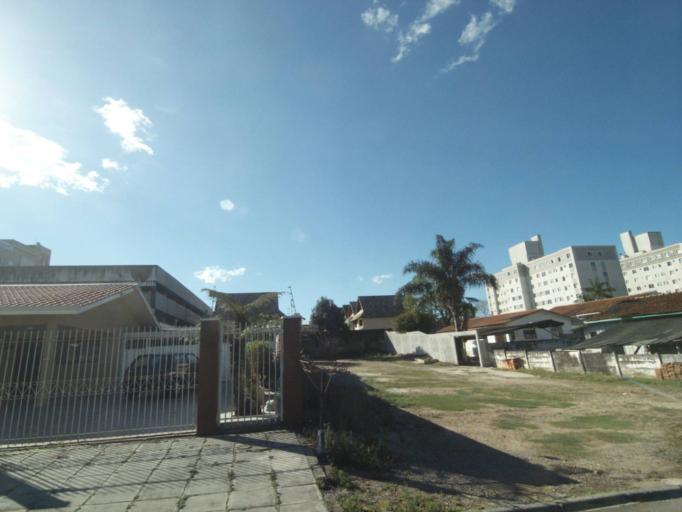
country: BR
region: Parana
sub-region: Curitiba
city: Curitiba
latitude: -25.3832
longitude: -49.2334
